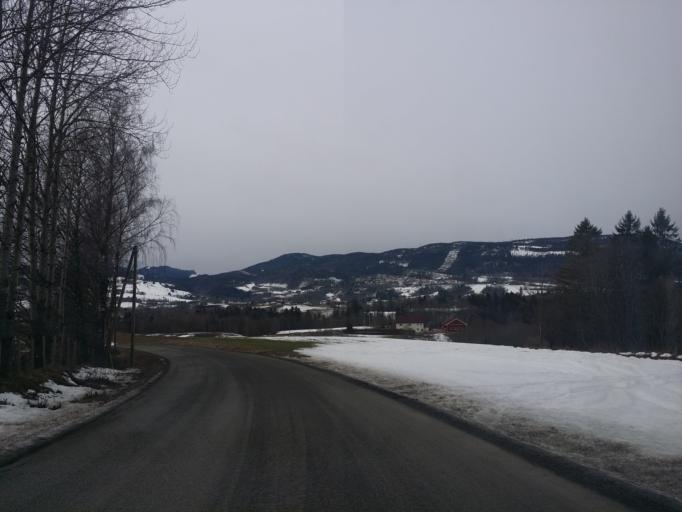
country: NO
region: Buskerud
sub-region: Lier
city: Tranby
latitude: 59.8529
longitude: 10.2714
